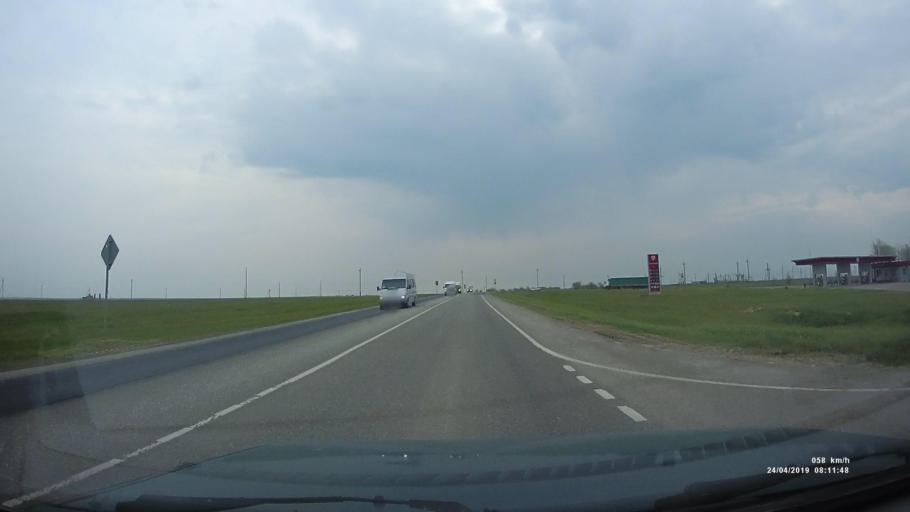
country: RU
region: Kalmykiya
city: Priyutnoye
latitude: 46.1030
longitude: 43.5323
